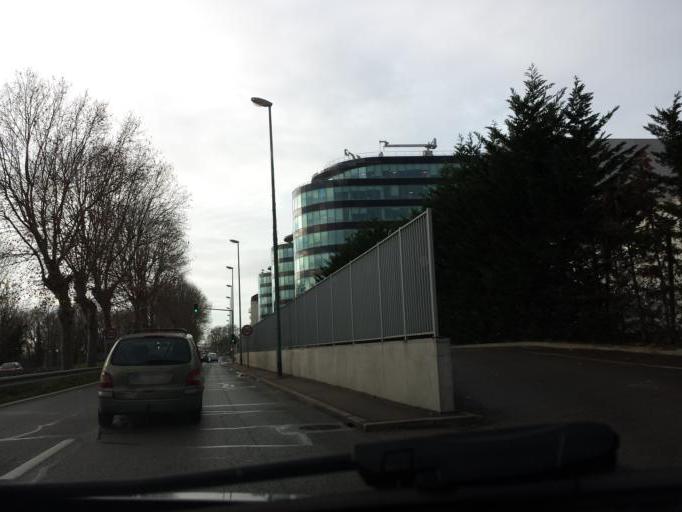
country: FR
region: Ile-de-France
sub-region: Departement du Val-d'Oise
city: Bezons
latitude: 48.9249
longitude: 2.2245
